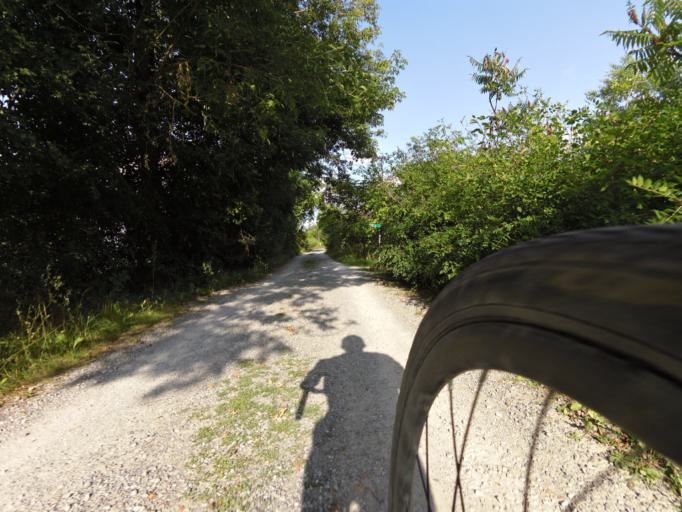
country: CA
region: Ontario
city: Kingston
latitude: 44.4267
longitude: -76.5625
